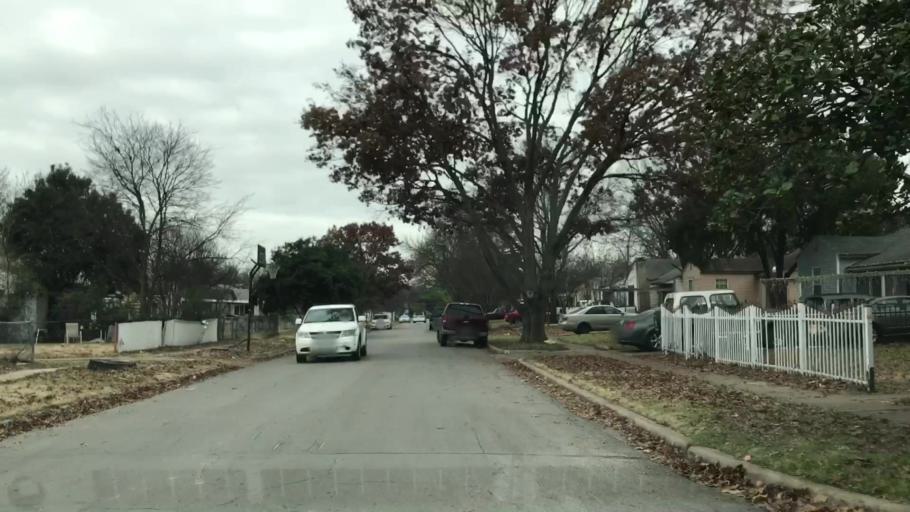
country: US
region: Texas
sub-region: Dallas County
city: Cockrell Hill
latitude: 32.7315
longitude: -96.8493
